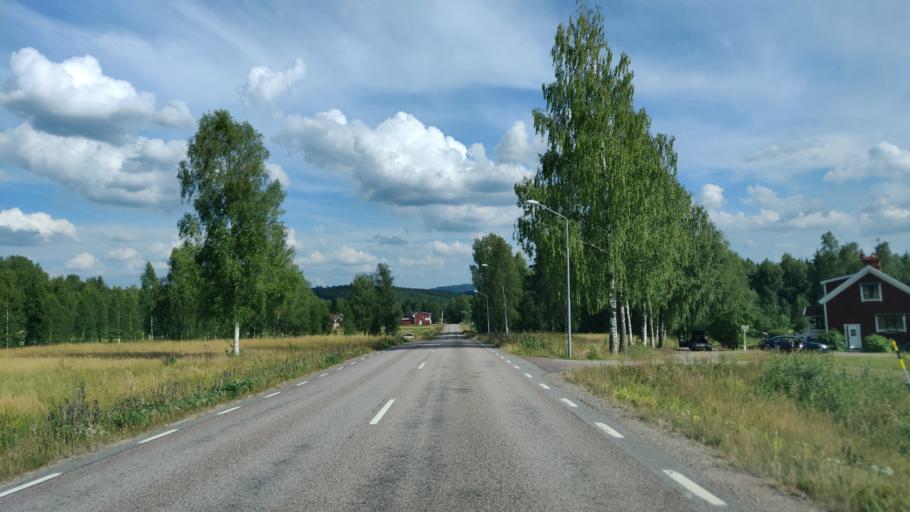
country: SE
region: Vaermland
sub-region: Hagfors Kommun
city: Hagfors
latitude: 60.0665
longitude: 13.6396
